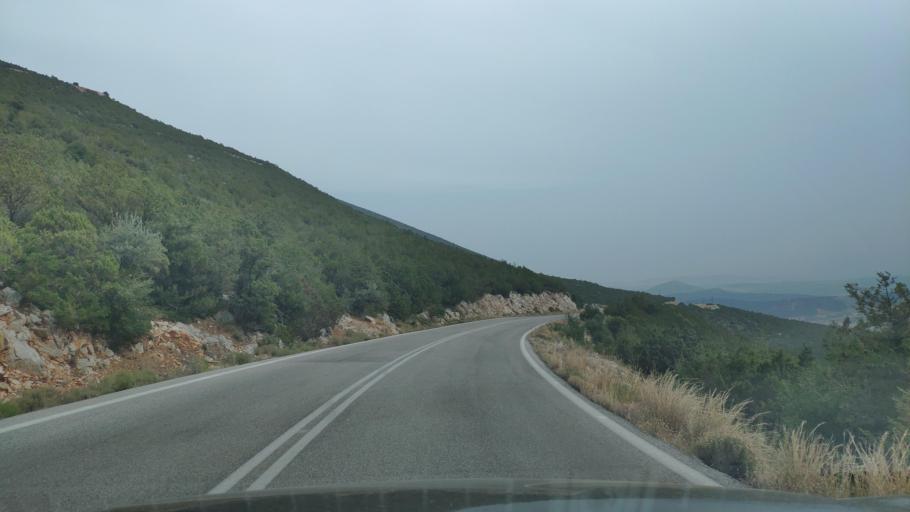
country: GR
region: Peloponnese
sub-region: Nomos Argolidos
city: Didyma
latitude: 37.4961
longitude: 23.1919
